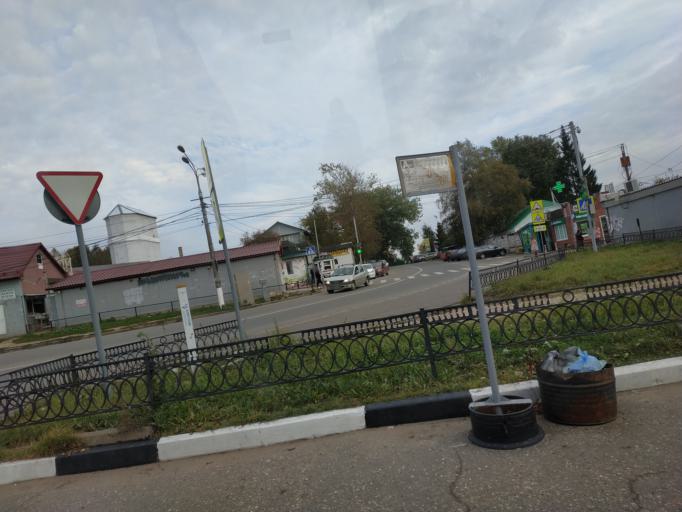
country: RU
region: Moskovskaya
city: Mozhaysk
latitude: 55.4953
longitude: 36.0316
